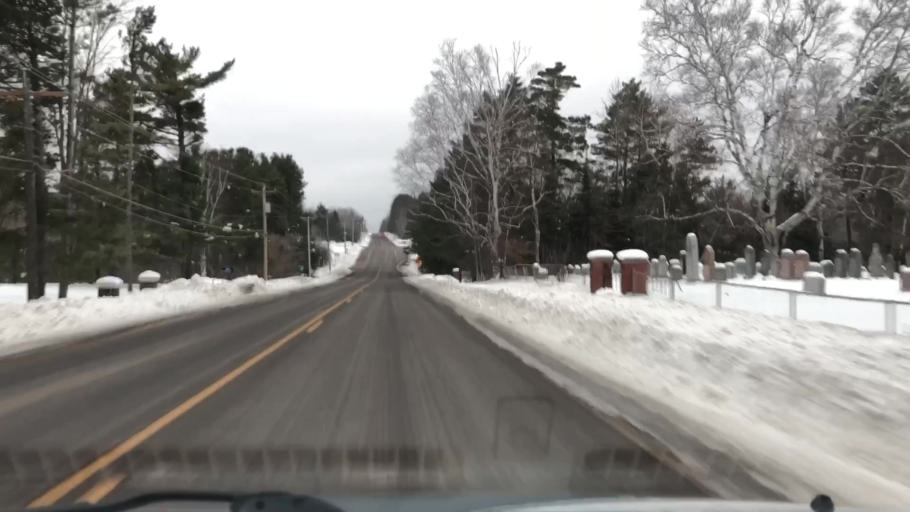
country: US
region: Minnesota
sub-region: Saint Louis County
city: Arnold
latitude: 46.8627
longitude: -92.1111
